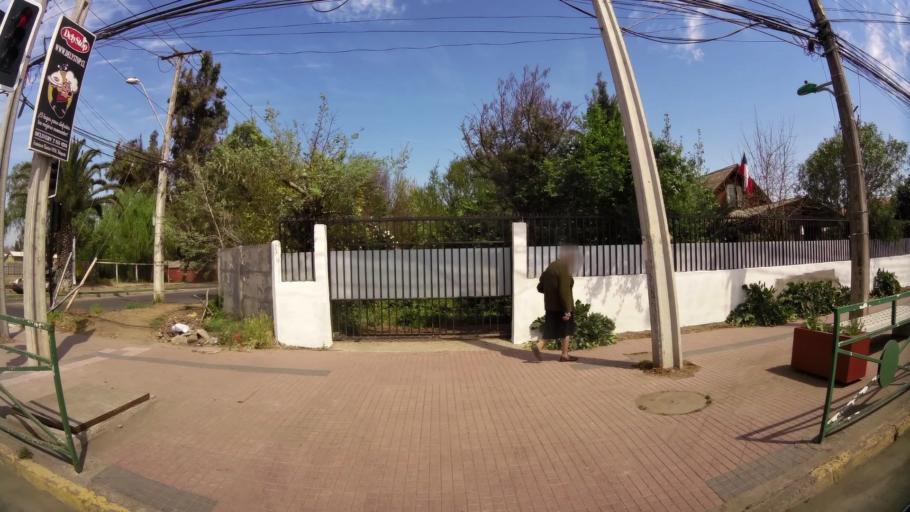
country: CL
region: Santiago Metropolitan
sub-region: Provincia de Talagante
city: Talagante
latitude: -33.6673
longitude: -70.9216
